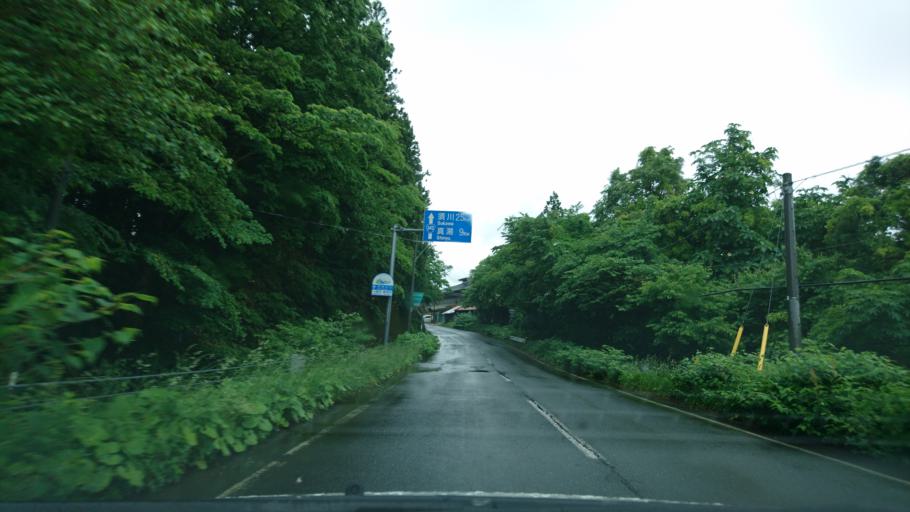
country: JP
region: Iwate
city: Ichinoseki
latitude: 38.9762
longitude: 140.9288
